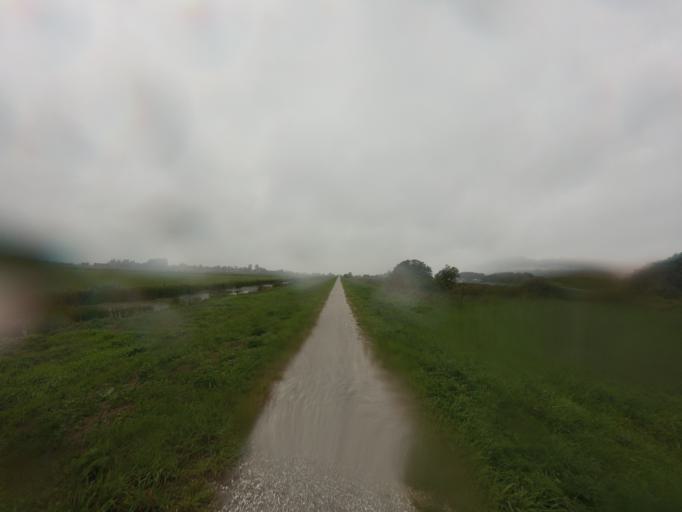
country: NL
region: Friesland
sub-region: Gemeente Smallingerland
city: Oudega
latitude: 53.1019
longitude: 5.9619
